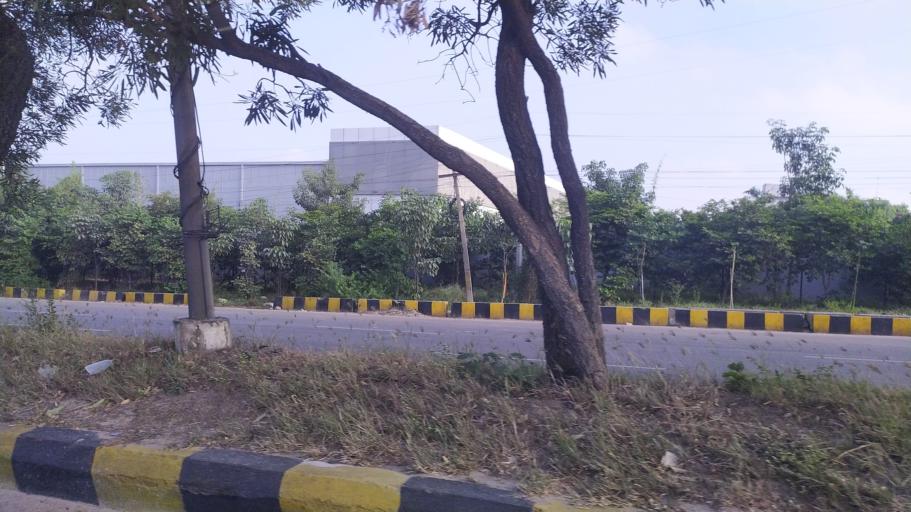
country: IN
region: Telangana
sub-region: Rangareddi
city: Balapur
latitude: 17.3175
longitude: 78.4384
